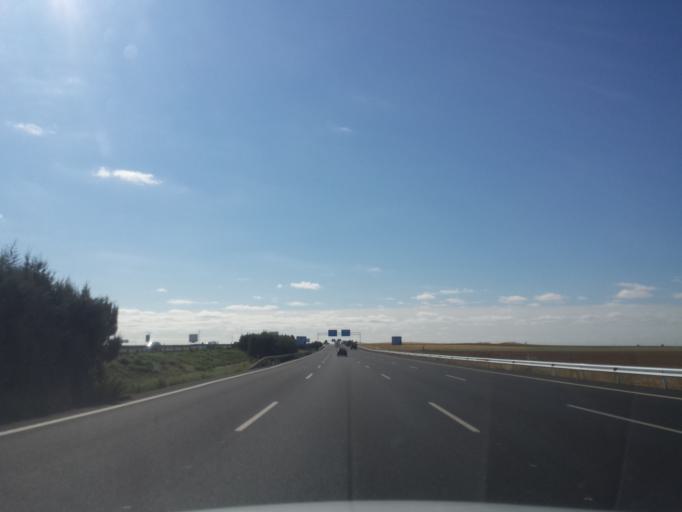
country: ES
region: Castille and Leon
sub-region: Provincia de Zamora
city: Castrogonzalo
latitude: 41.9755
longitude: -5.6070
